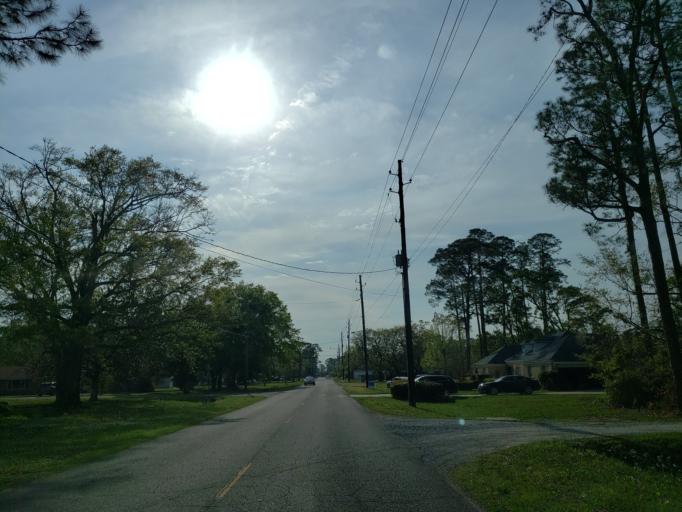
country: US
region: Mississippi
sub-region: Harrison County
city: West Gulfport
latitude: 30.4093
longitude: -89.0468
